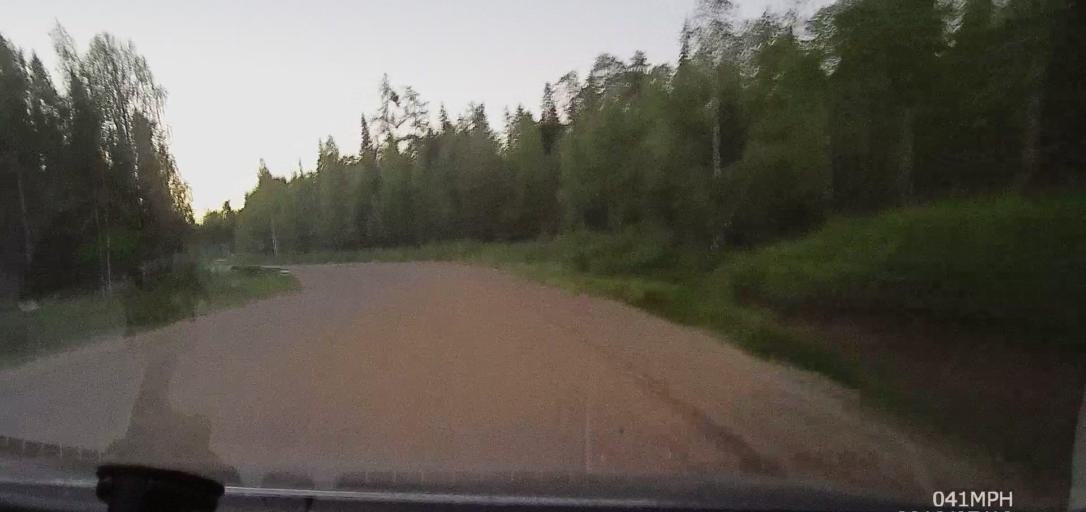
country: RU
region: Arkhangelskaya
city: Pinega
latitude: 64.4358
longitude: 43.1449
